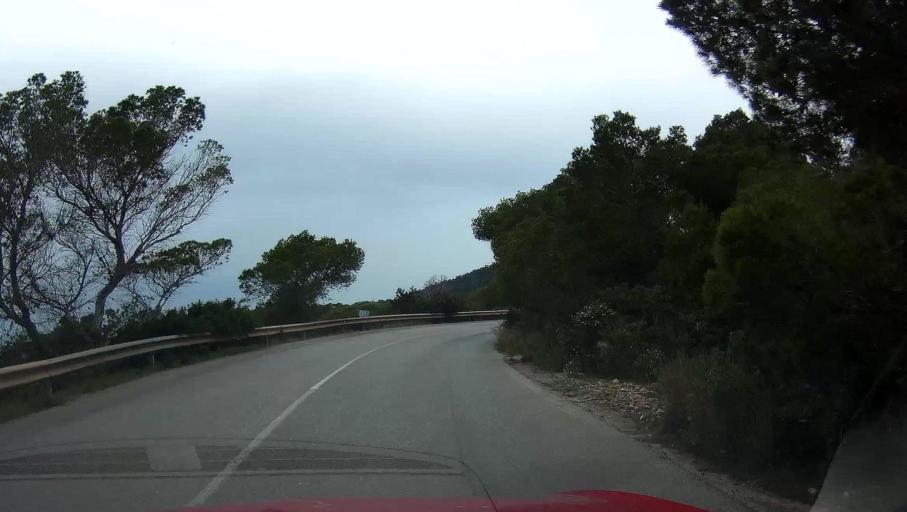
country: ES
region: Balearic Islands
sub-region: Illes Balears
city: Sant Josep de sa Talaia
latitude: 38.8692
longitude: 1.3371
